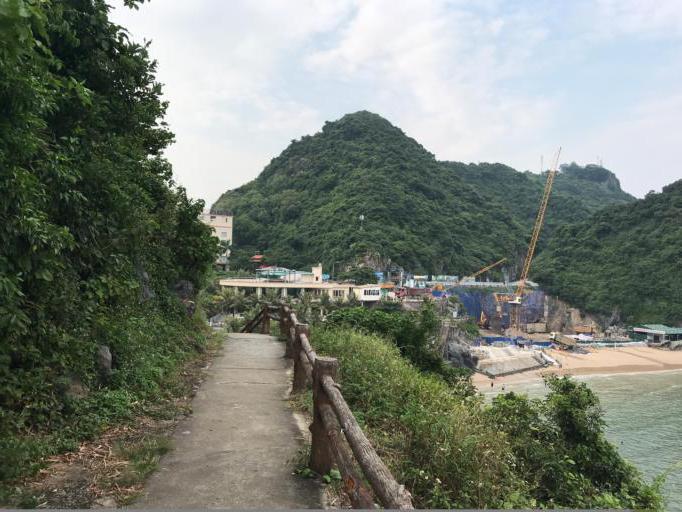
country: VN
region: Hai Phong
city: Cat Ba
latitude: 20.7164
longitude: 107.0523
